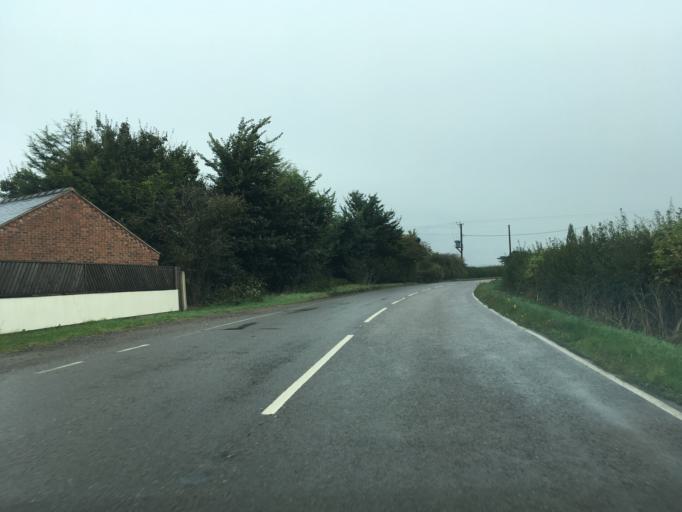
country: GB
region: England
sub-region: Nottinghamshire
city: East Leake
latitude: 52.8540
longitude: -1.1749
